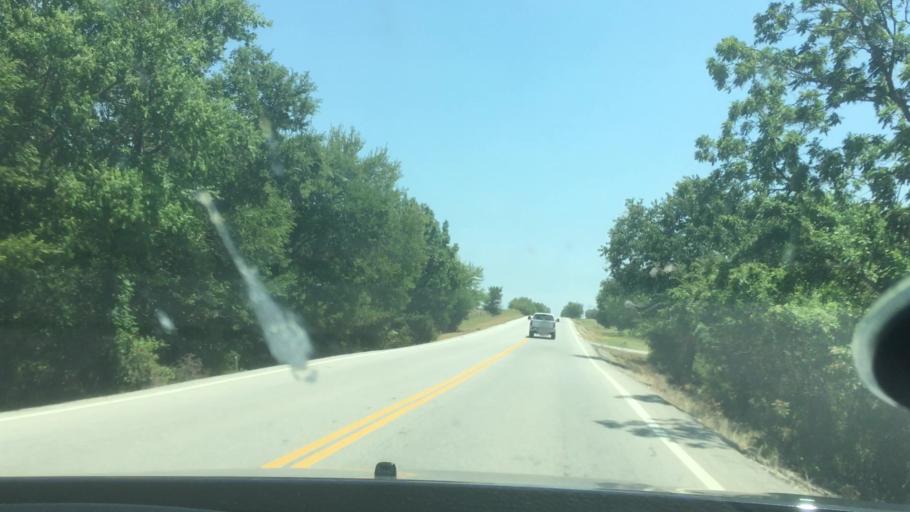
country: US
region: Oklahoma
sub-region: Bryan County
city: Durant
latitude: 34.1643
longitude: -96.3994
